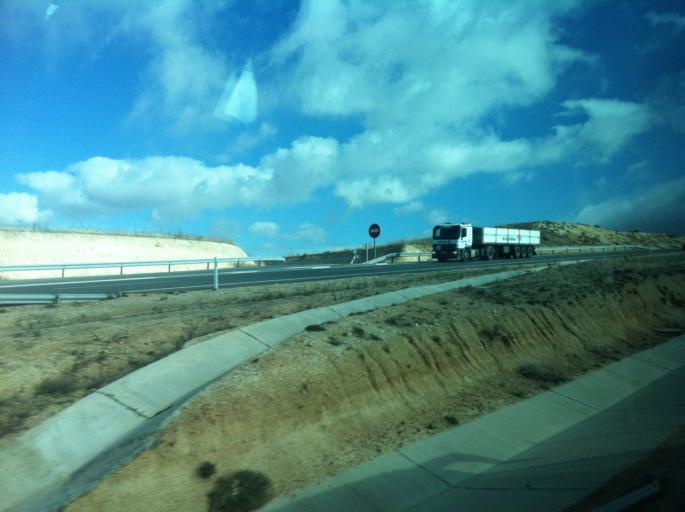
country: ES
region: Castille and Leon
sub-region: Provincia de Burgos
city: Bahabon de Esgueva
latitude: 41.8520
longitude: -3.7237
